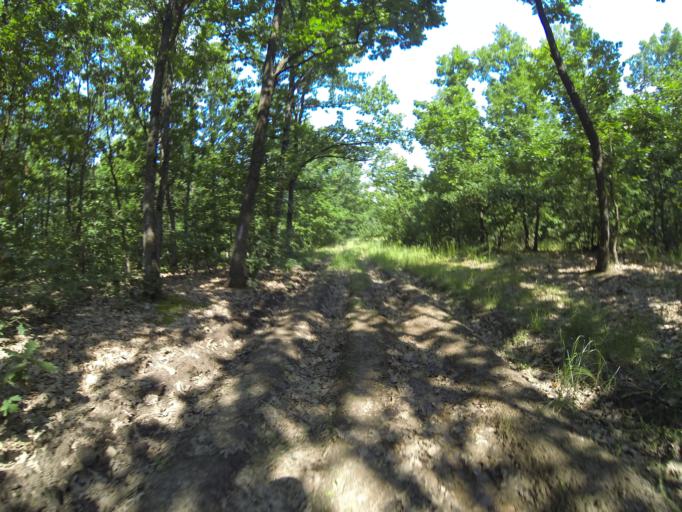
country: RO
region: Gorj
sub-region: Comuna Crusetu
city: Crusetu
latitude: 44.6136
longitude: 23.6420
